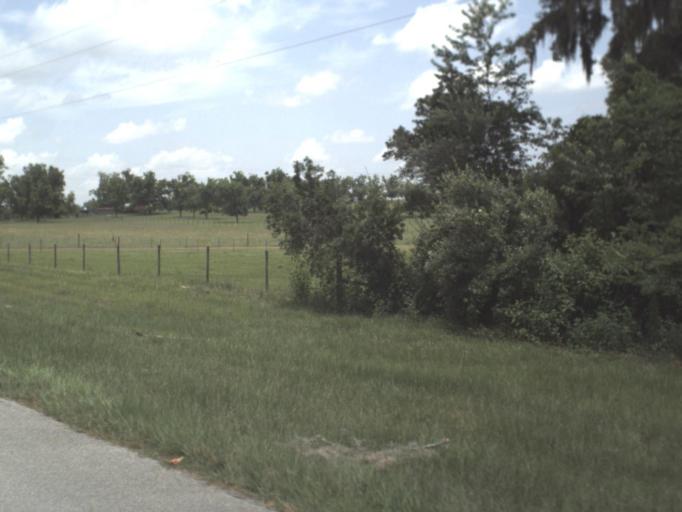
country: US
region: Florida
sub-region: Madison County
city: Madison
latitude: 30.5018
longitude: -83.4234
